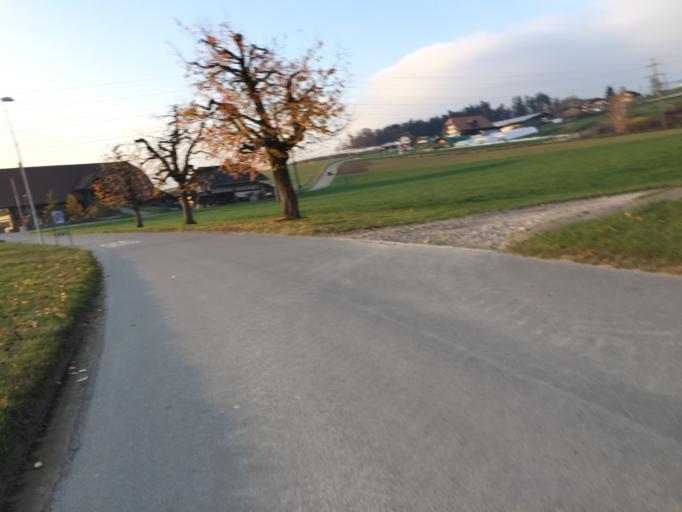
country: CH
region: Bern
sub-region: Bern-Mittelland District
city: Taegertschi
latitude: 46.8773
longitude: 7.5828
